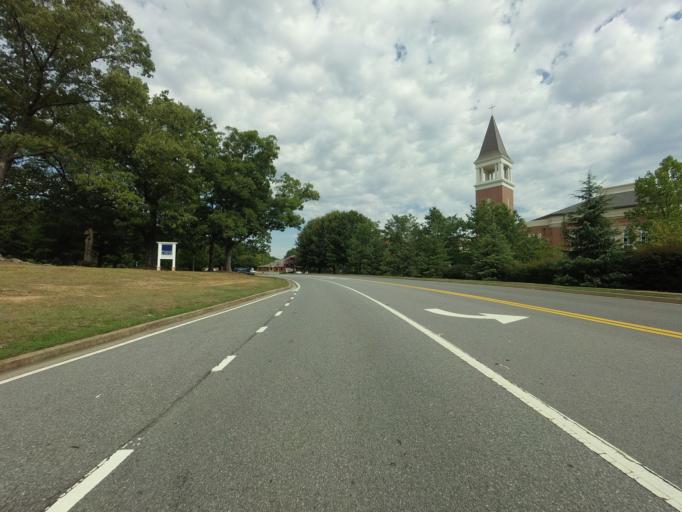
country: US
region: Georgia
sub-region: Fulton County
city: Johns Creek
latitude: 34.0499
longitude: -84.1730
